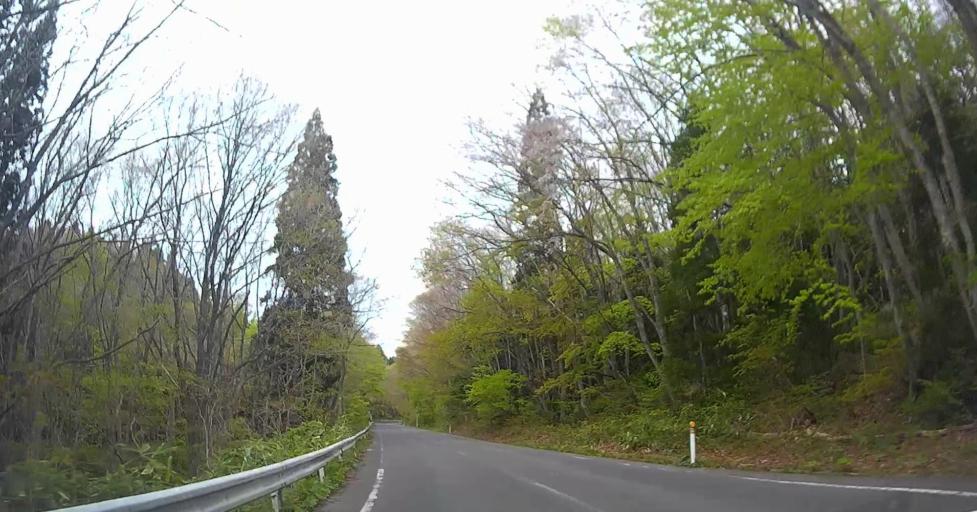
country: JP
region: Aomori
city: Goshogawara
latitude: 40.9046
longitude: 140.5229
